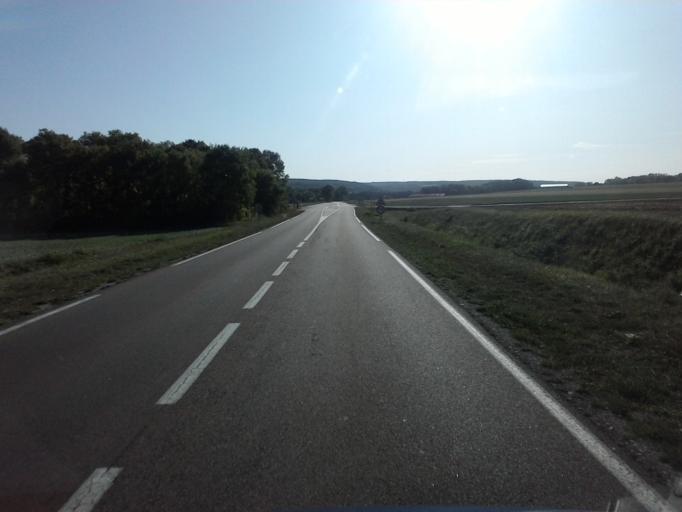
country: FR
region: Champagne-Ardenne
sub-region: Departement de l'Aube
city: Bar-sur-Seine
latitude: 48.1265
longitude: 4.3564
